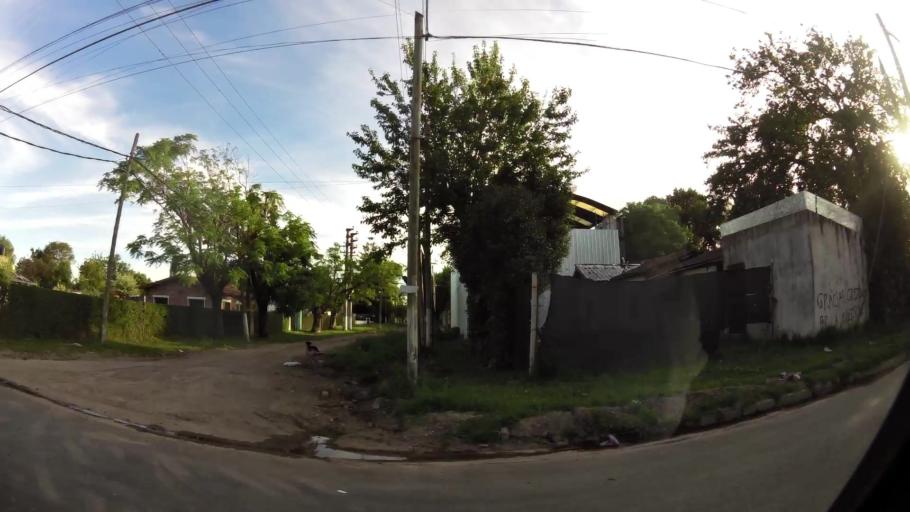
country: AR
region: Buenos Aires
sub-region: Partido de Almirante Brown
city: Adrogue
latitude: -34.7983
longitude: -58.3310
